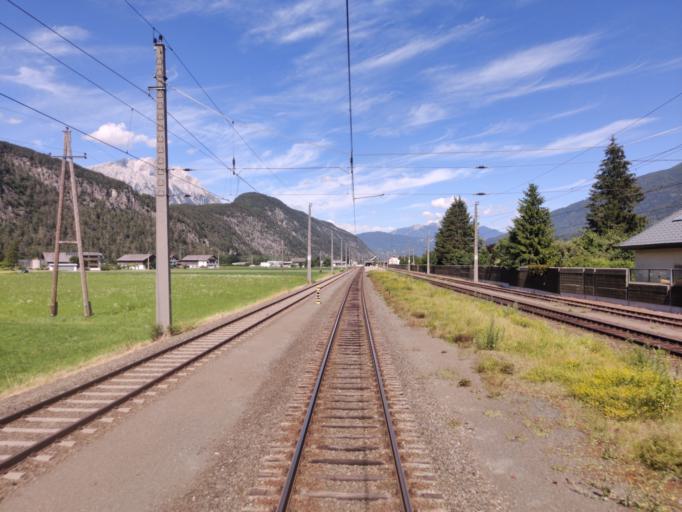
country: AT
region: Tyrol
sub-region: Politischer Bezirk Imst
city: Stams
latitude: 47.2804
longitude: 10.9740
